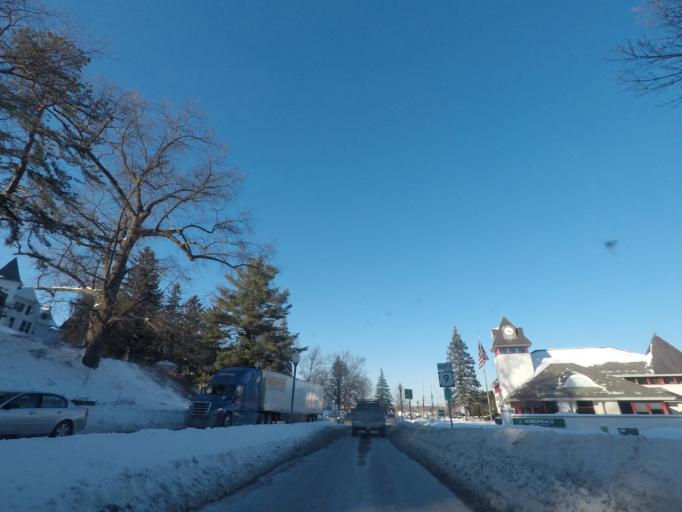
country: US
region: New York
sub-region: Saratoga County
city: Saratoga Springs
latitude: 43.0679
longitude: -73.7891
